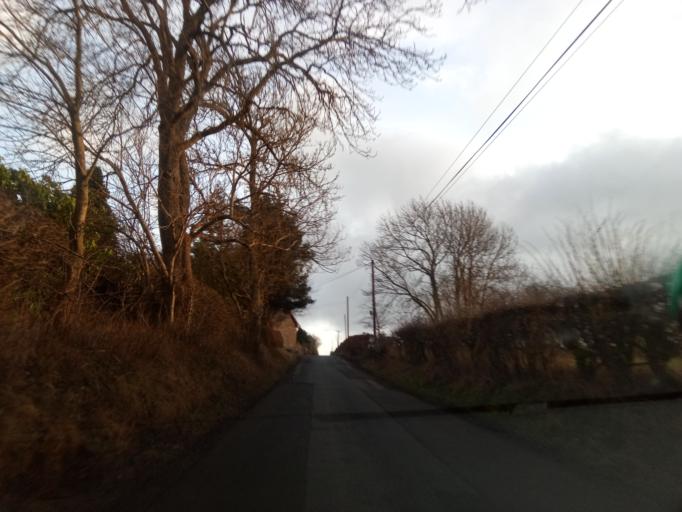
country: GB
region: Scotland
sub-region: The Scottish Borders
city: Selkirk
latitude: 55.5712
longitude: -2.8136
